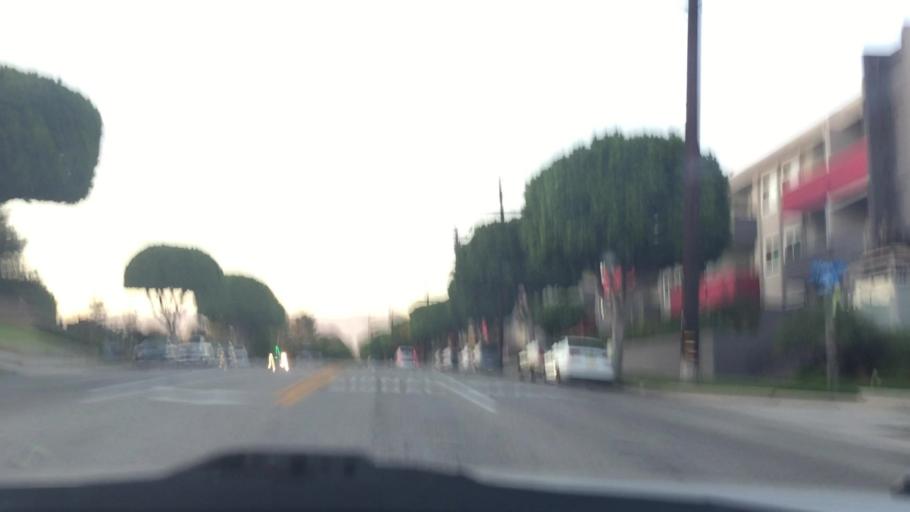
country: US
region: California
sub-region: Los Angeles County
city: Monterey Park
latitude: 34.0533
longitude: -118.1265
